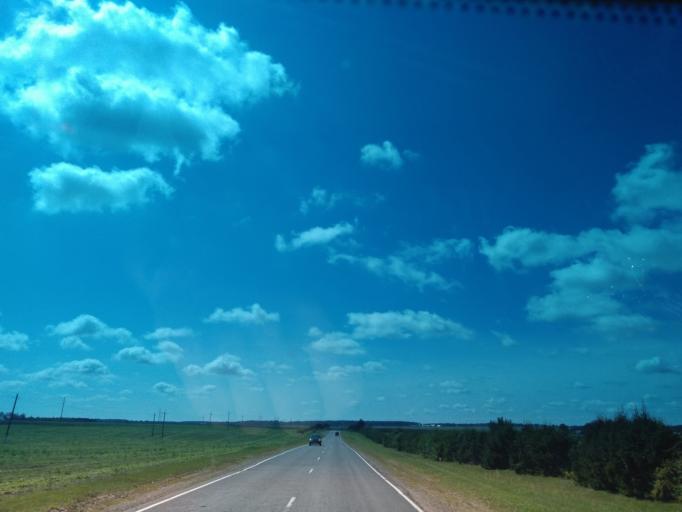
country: BY
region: Minsk
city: Uzda
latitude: 53.3796
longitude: 27.2387
